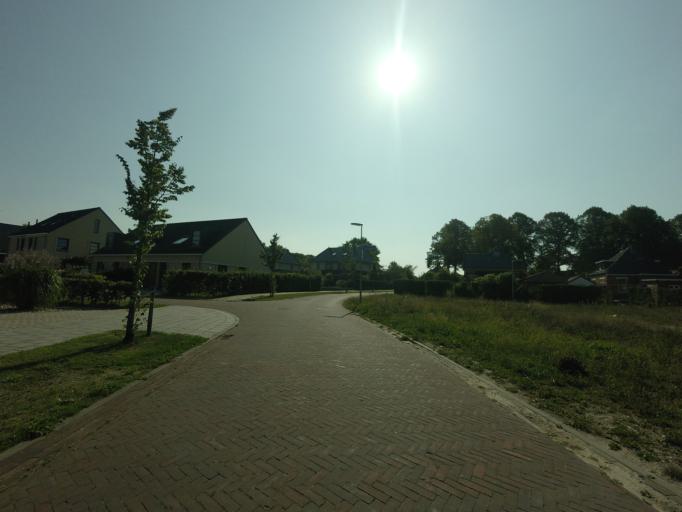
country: NL
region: Groningen
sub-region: Gemeente Zuidhorn
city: Zuidhorn
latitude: 53.2430
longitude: 6.4102
